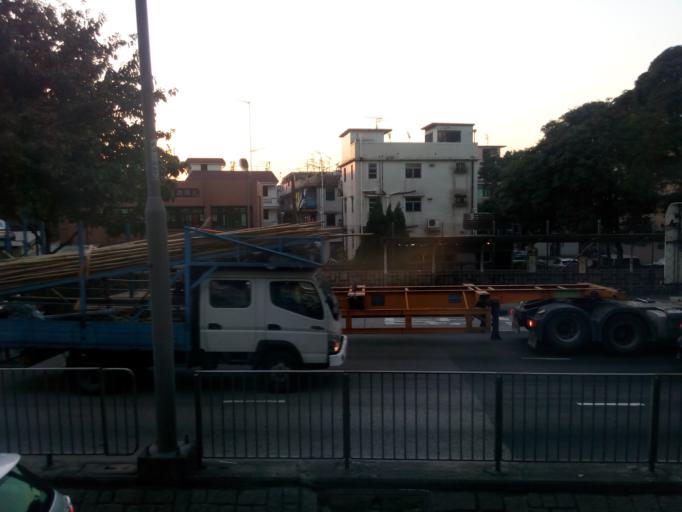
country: HK
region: Tai Po
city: Tai Po
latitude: 22.5023
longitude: 114.1234
